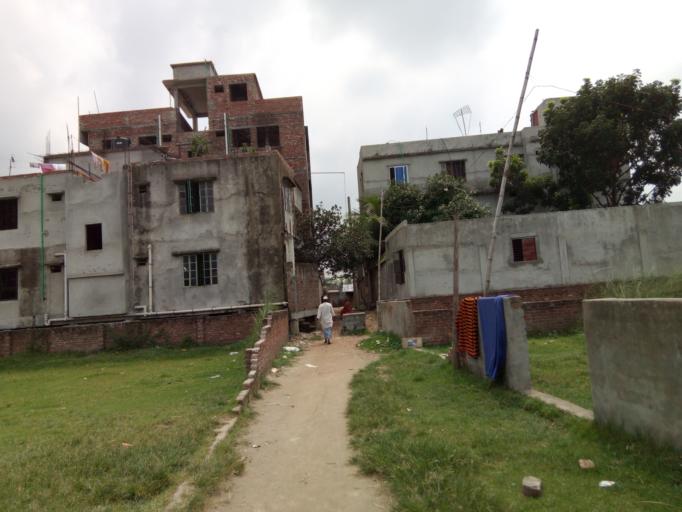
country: BD
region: Dhaka
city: Paltan
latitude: 23.7504
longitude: 90.4501
